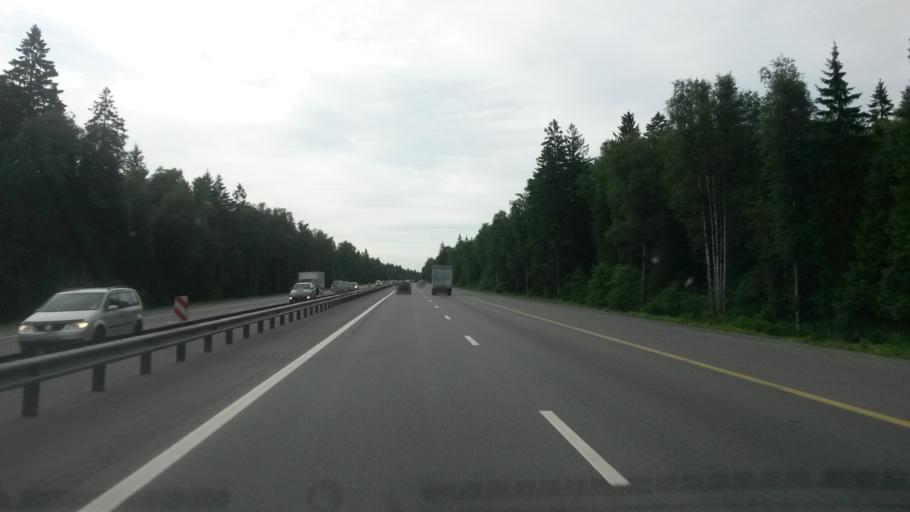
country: RU
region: Moskovskaya
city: Ashukino
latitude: 56.1619
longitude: 38.0145
